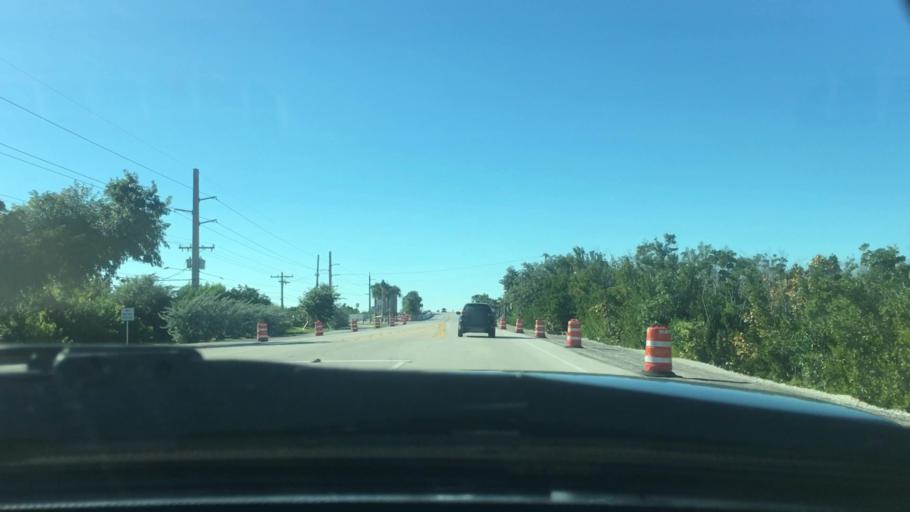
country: US
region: Florida
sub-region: Monroe County
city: Cudjoe Key
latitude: 24.6631
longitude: -81.4620
